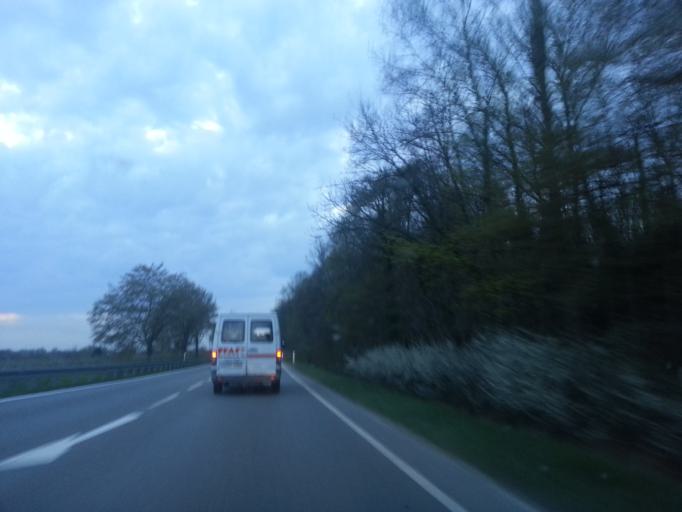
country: DE
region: Baden-Wuerttemberg
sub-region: Tuebingen Region
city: Eriskirch
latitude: 47.6353
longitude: 9.5230
